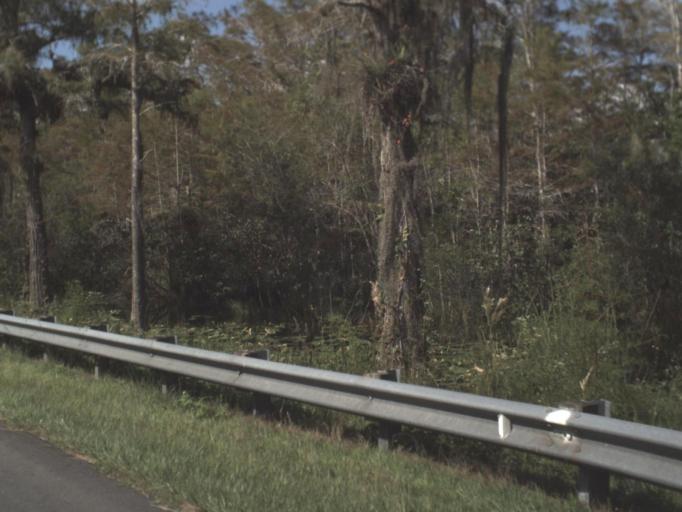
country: US
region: Florida
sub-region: Miami-Dade County
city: Kendall West
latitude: 25.8416
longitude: -80.9152
